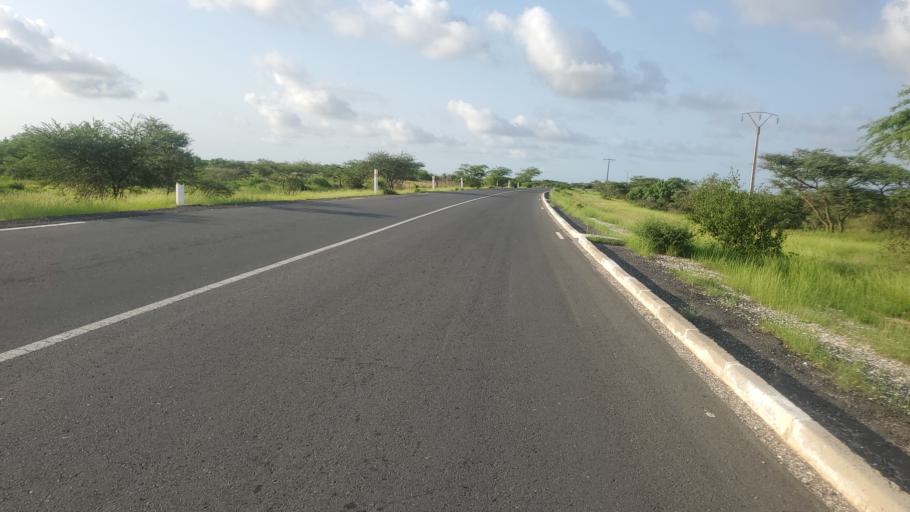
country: SN
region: Saint-Louis
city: Saint-Louis
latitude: 16.1200
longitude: -16.4143
